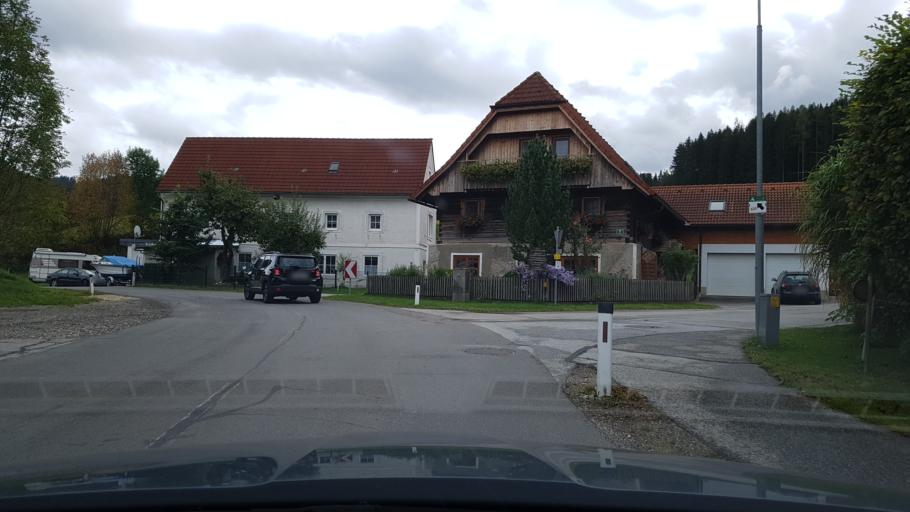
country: AT
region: Styria
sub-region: Politischer Bezirk Bruck-Muerzzuschlag
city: Allerheiligen im Muerztal
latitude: 47.4753
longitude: 15.4111
